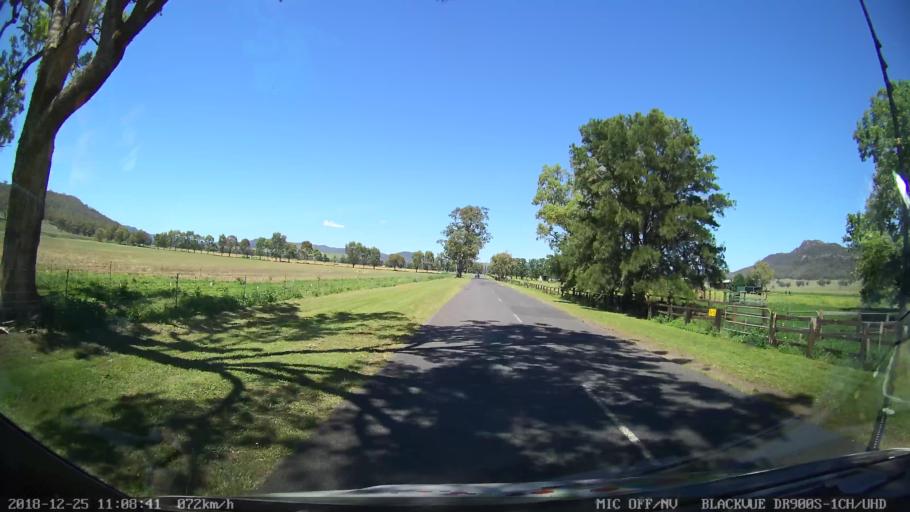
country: AU
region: New South Wales
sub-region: Upper Hunter Shire
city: Merriwa
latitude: -32.4041
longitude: 150.1229
